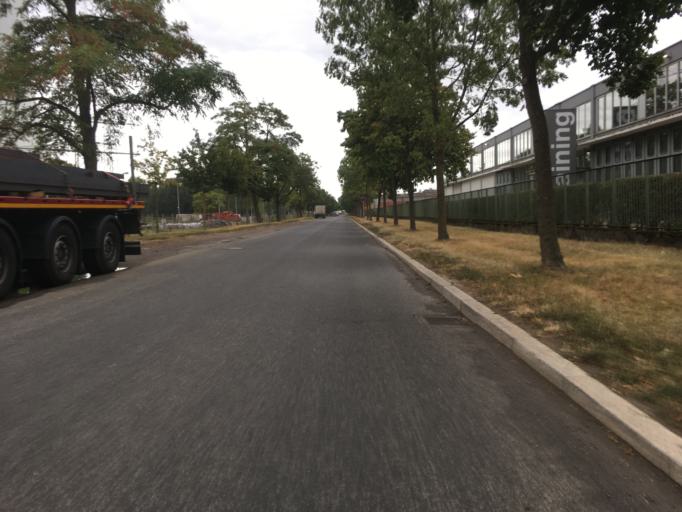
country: DE
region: Baden-Wuerttemberg
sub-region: Regierungsbezirk Stuttgart
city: Neckarsulm
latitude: 49.1763
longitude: 9.2097
